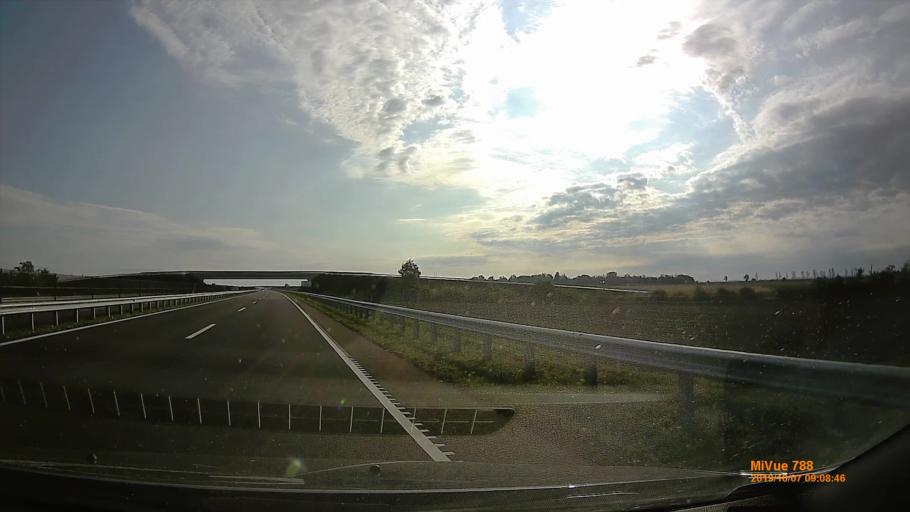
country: HU
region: Bekes
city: Szarvas
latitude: 46.8147
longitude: 20.6300
